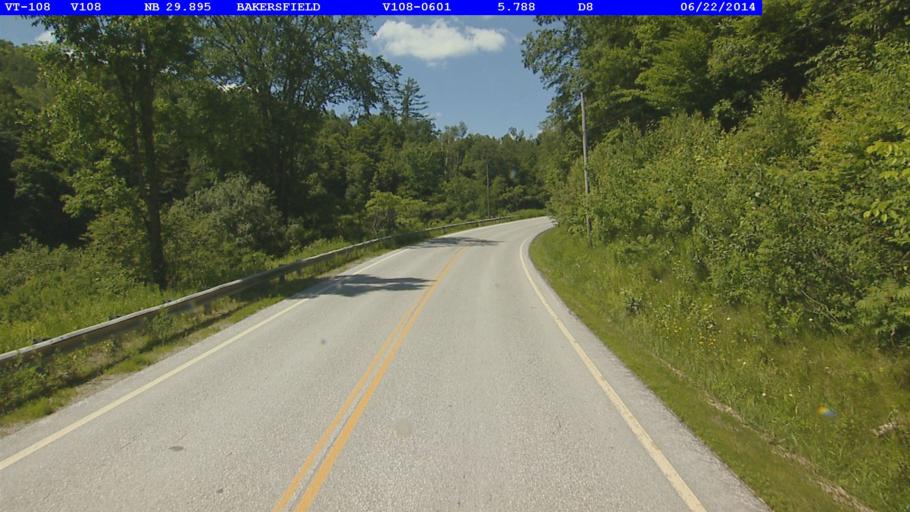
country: US
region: Vermont
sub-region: Franklin County
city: Enosburg Falls
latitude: 44.8098
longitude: -72.7896
